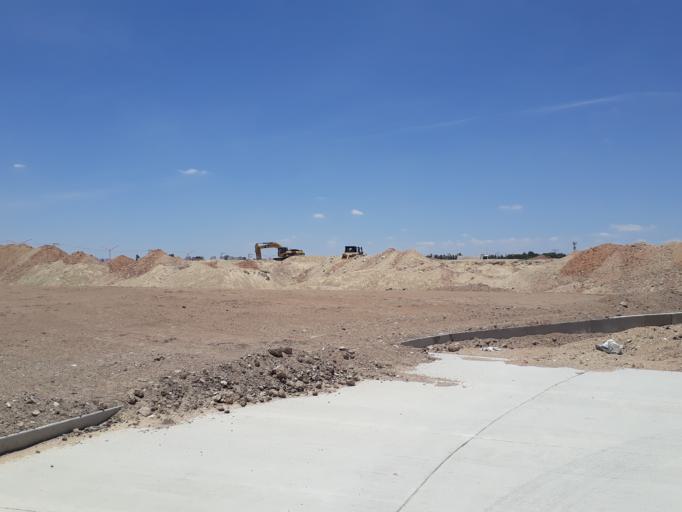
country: MX
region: Aguascalientes
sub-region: Aguascalientes
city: San Sebastian [Fraccionamiento]
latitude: 21.8023
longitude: -102.3017
